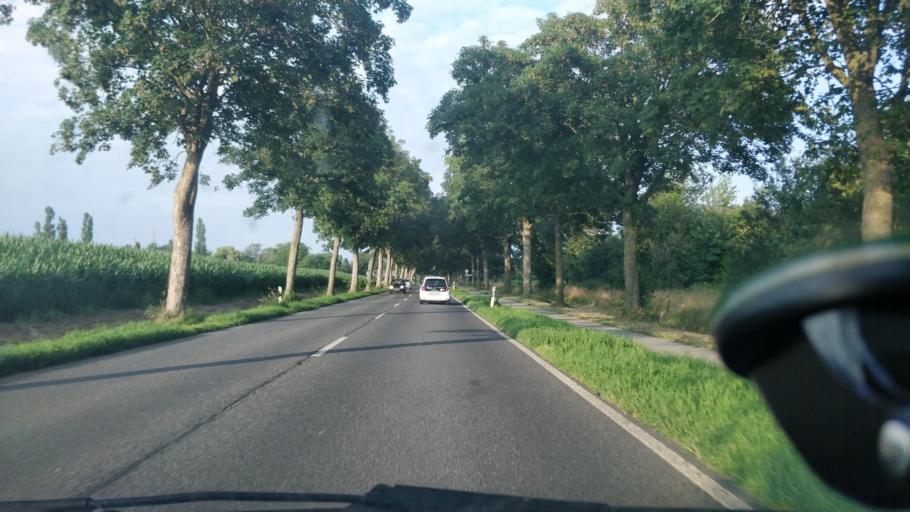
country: DE
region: North Rhine-Westphalia
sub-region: Regierungsbezirk Dusseldorf
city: Rheurdt
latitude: 51.4636
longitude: 6.4415
